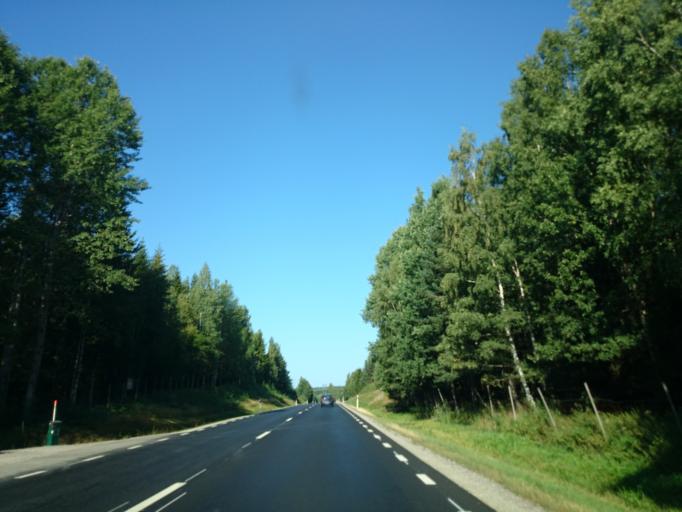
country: SE
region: Gaevleborg
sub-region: Hudiksvalls Kommun
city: Sorforsa
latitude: 61.7380
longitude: 16.9136
